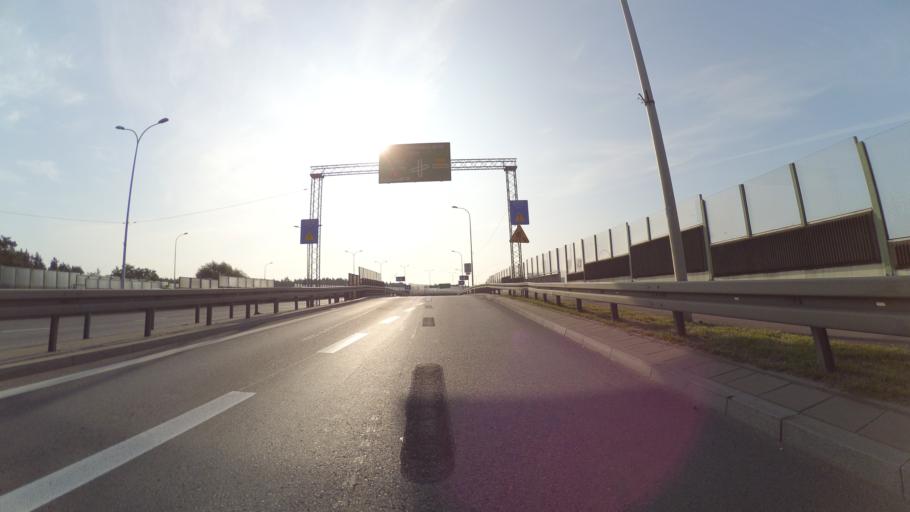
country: PL
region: Podlasie
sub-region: Bialystok
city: Bialystok
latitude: 53.1594
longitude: 23.1485
